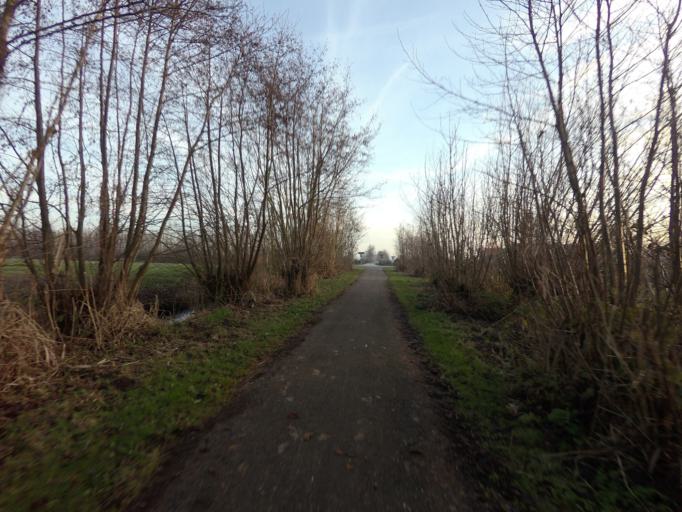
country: NL
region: Utrecht
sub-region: Gemeente Woerden
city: Woerden
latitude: 52.1386
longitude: 4.9347
